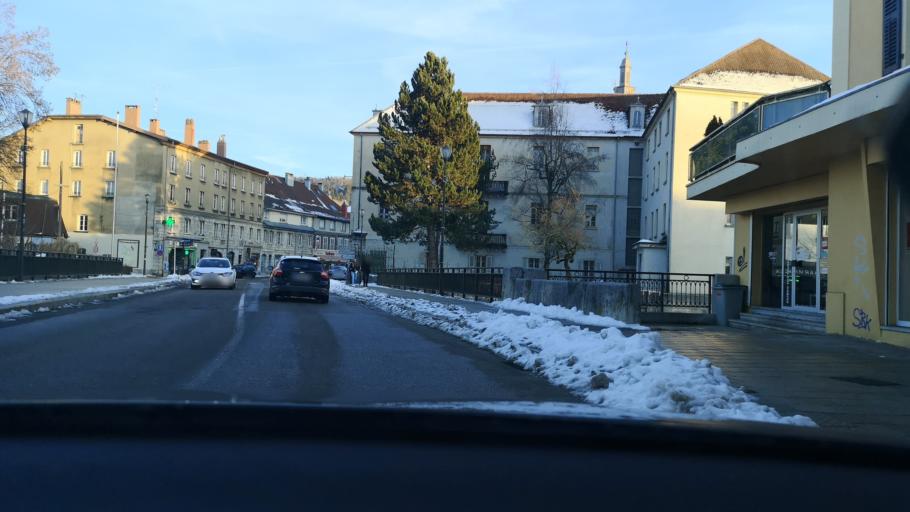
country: FR
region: Franche-Comte
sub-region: Departement du Doubs
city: Pontarlier
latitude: 46.9023
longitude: 6.3584
